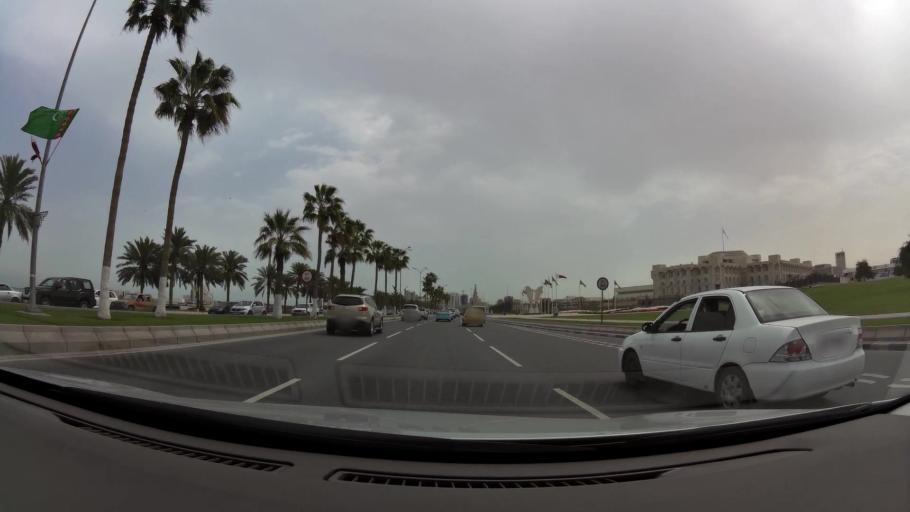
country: QA
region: Baladiyat ad Dawhah
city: Doha
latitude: 25.2940
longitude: 51.5254
